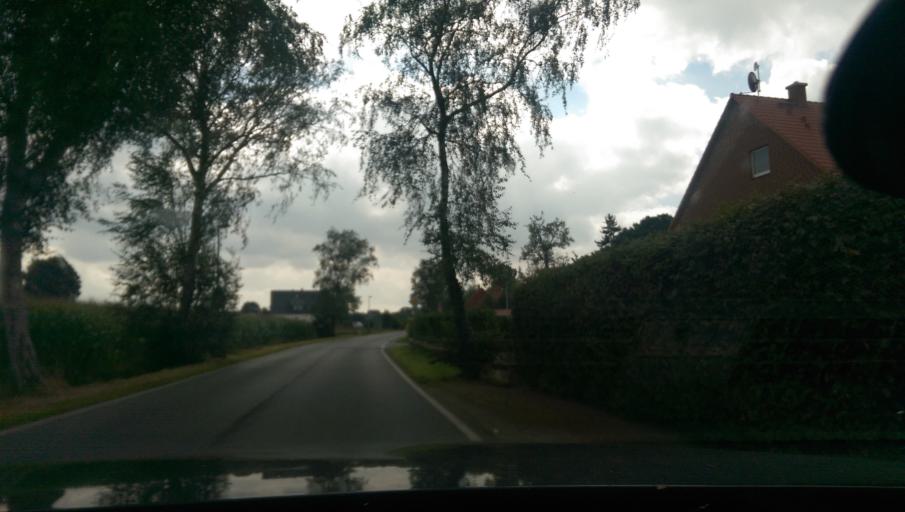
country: DE
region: Lower Saxony
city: Steimbke
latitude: 52.6151
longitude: 9.4834
